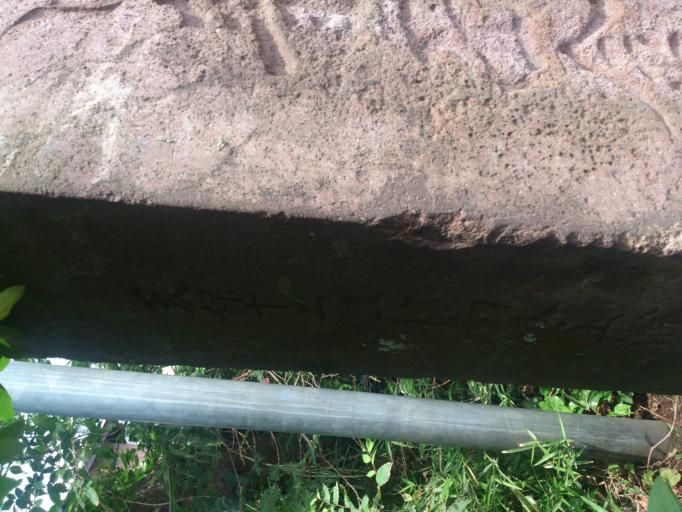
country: JP
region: Chiba
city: Matsudo
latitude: 35.8015
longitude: 139.9348
